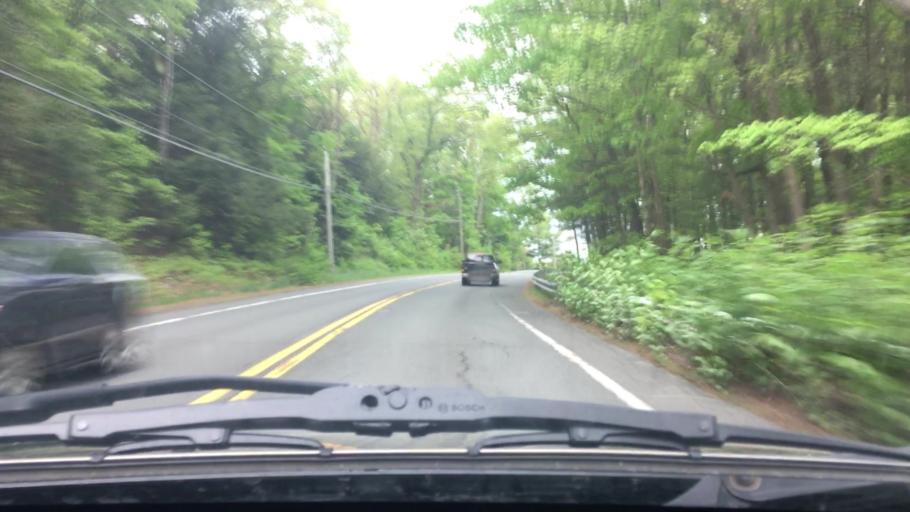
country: US
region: Massachusetts
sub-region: Franklin County
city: Leverett
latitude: 42.4581
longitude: -72.5211
